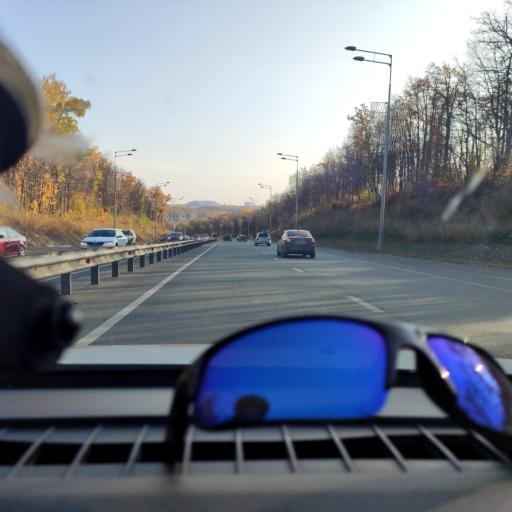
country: RU
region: Samara
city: Novosemeykino
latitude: 53.3167
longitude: 50.2301
